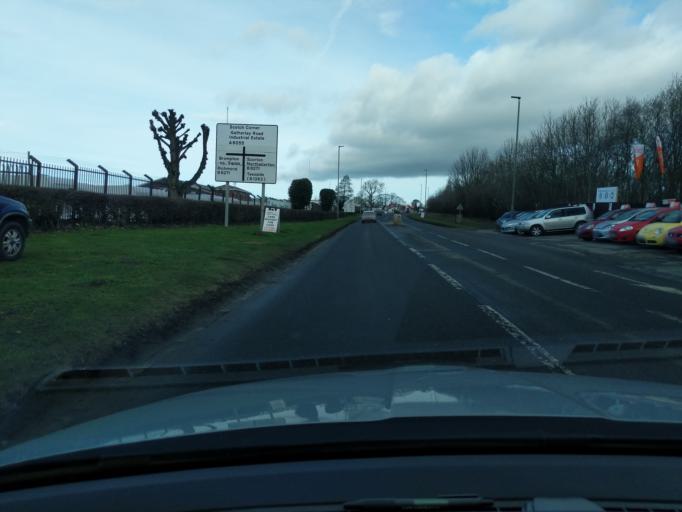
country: GB
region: England
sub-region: North Yorkshire
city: Catterick
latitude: 54.3917
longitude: -1.6528
